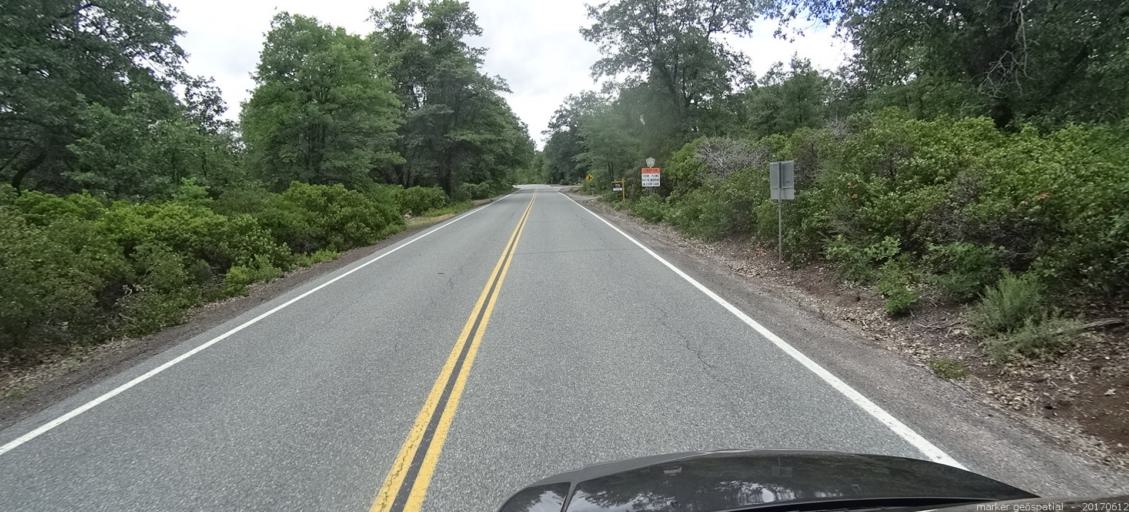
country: US
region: California
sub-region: Siskiyou County
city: Mount Shasta
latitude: 41.3278
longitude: -122.3063
